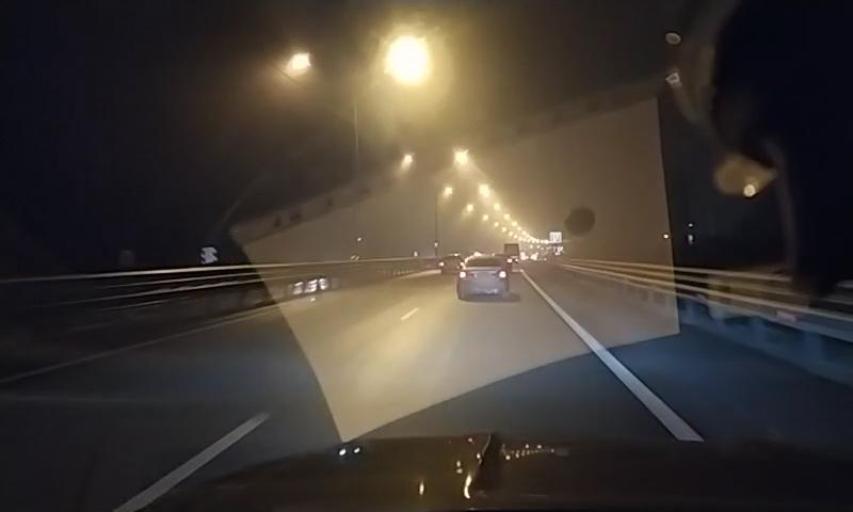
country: RU
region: Leningrad
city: Bugry
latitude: 60.1214
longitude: 30.3849
